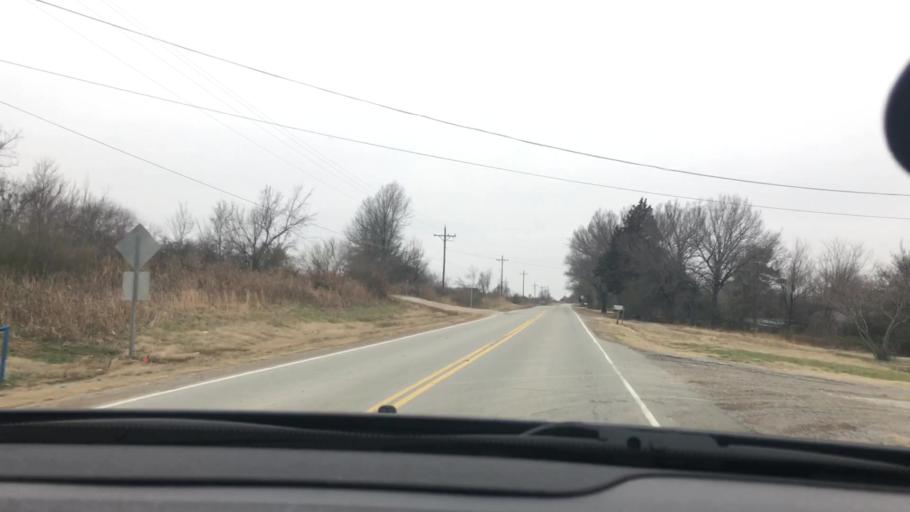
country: US
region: Oklahoma
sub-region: Coal County
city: Coalgate
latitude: 34.5398
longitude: -96.2311
